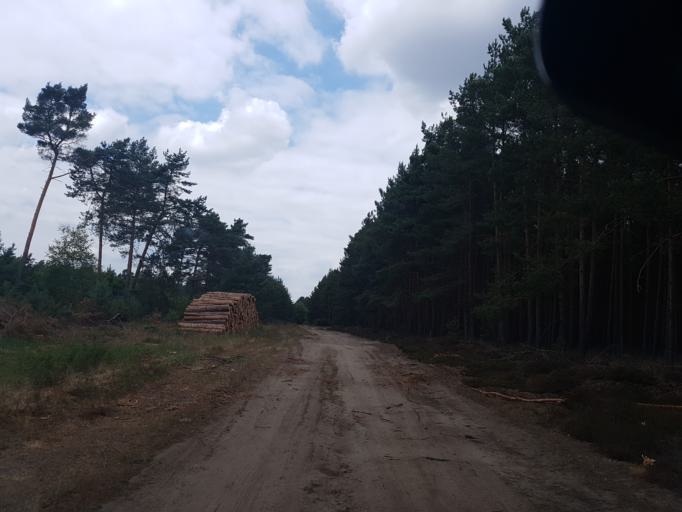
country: DE
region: Brandenburg
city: Treuenbrietzen
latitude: 52.0616
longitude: 12.8304
